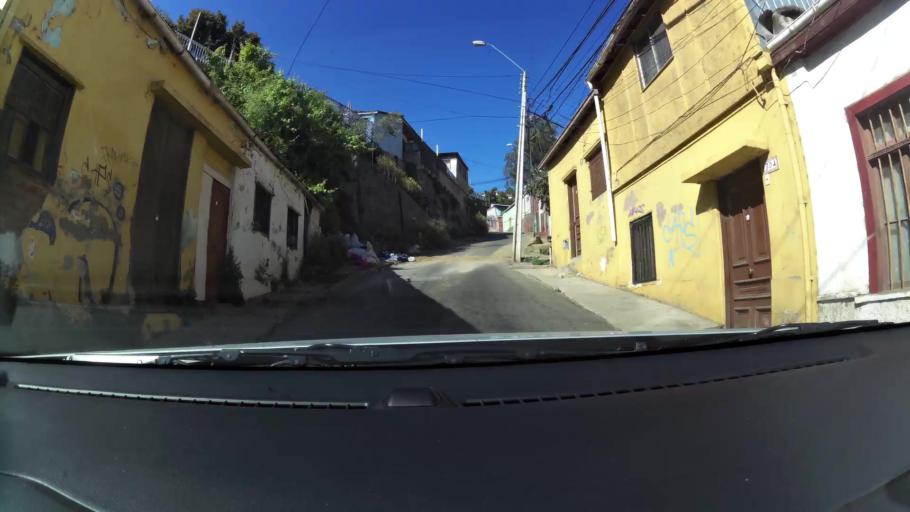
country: CL
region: Valparaiso
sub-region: Provincia de Valparaiso
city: Valparaiso
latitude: -33.0498
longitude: -71.6333
